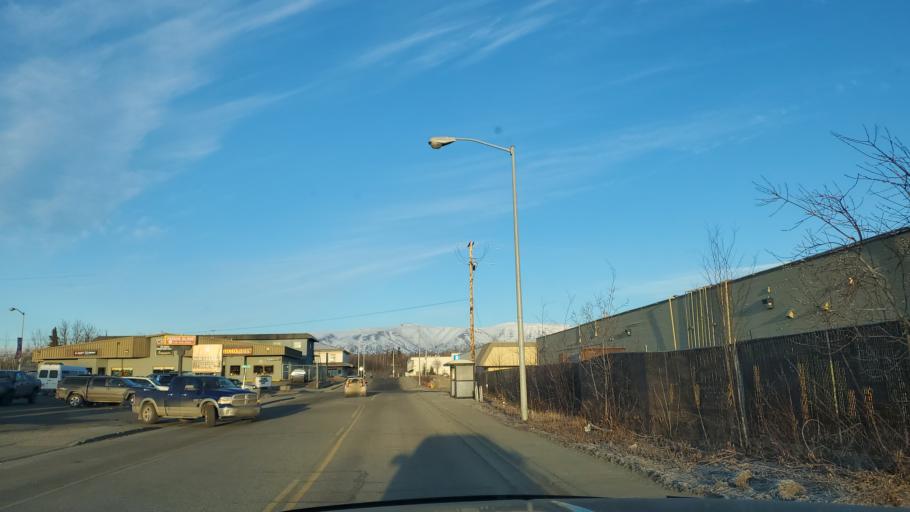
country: US
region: Alaska
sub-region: Matanuska-Susitna Borough
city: Wasilla
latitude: 61.5816
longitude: -149.4372
